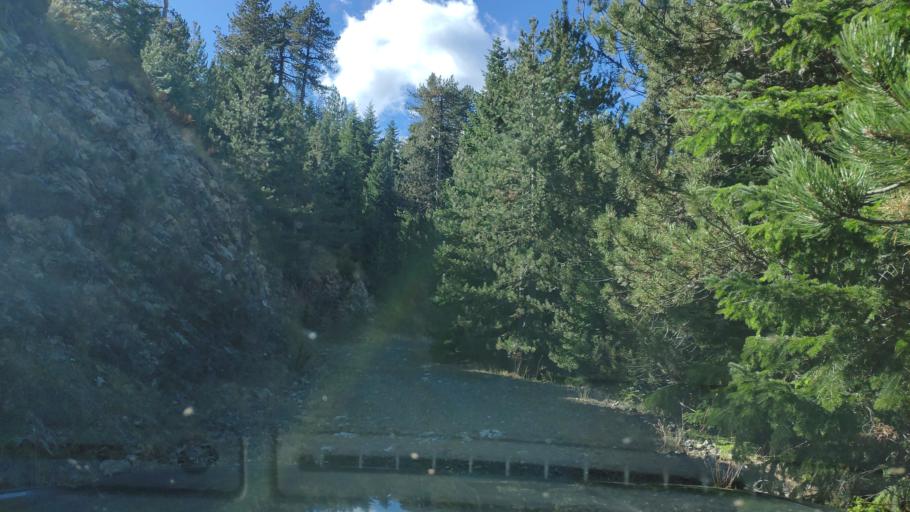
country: GR
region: Epirus
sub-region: Nomos Ioanninon
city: Metsovo
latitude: 39.8903
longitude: 21.2188
